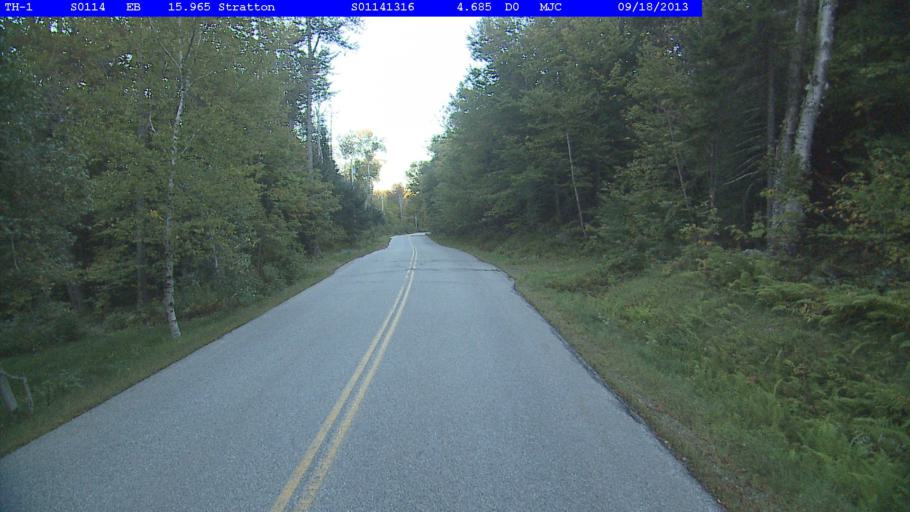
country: US
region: Vermont
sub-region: Windham County
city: Dover
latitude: 43.0473
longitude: -72.9189
